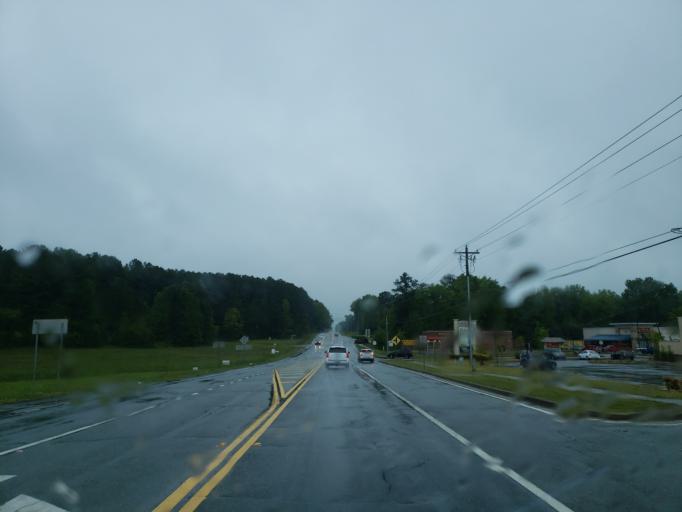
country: US
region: Georgia
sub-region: Carroll County
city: Villa Rica
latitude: 33.8094
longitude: -84.8892
